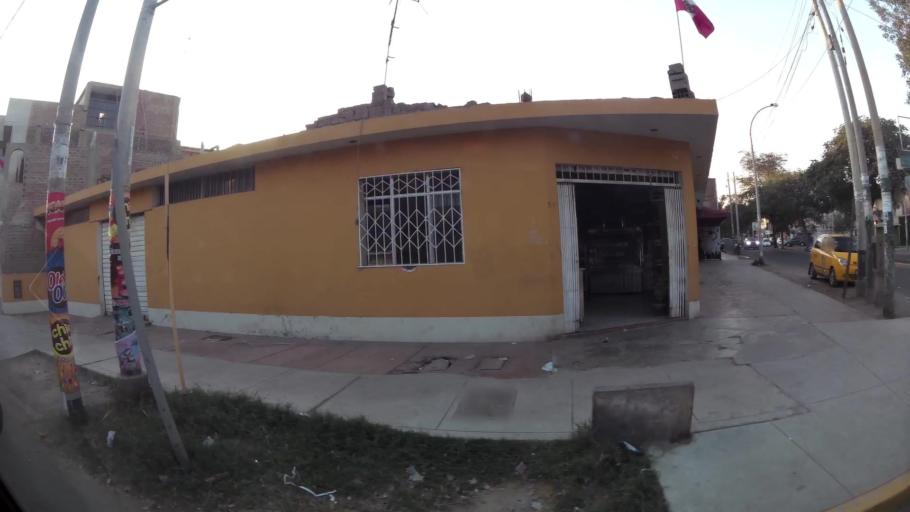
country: PE
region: Ica
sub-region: Provincia de Ica
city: Ica
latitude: -14.0803
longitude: -75.7264
